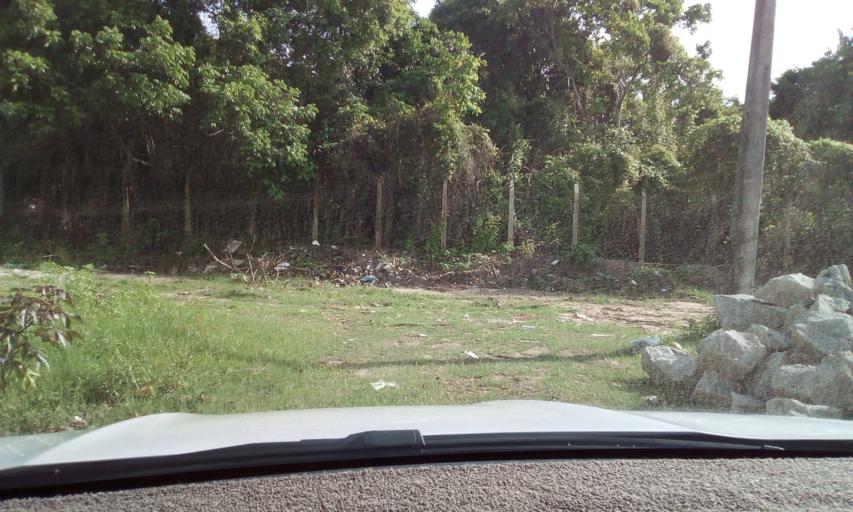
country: BR
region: Paraiba
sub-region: Joao Pessoa
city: Joao Pessoa
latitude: -7.1851
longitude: -34.8256
